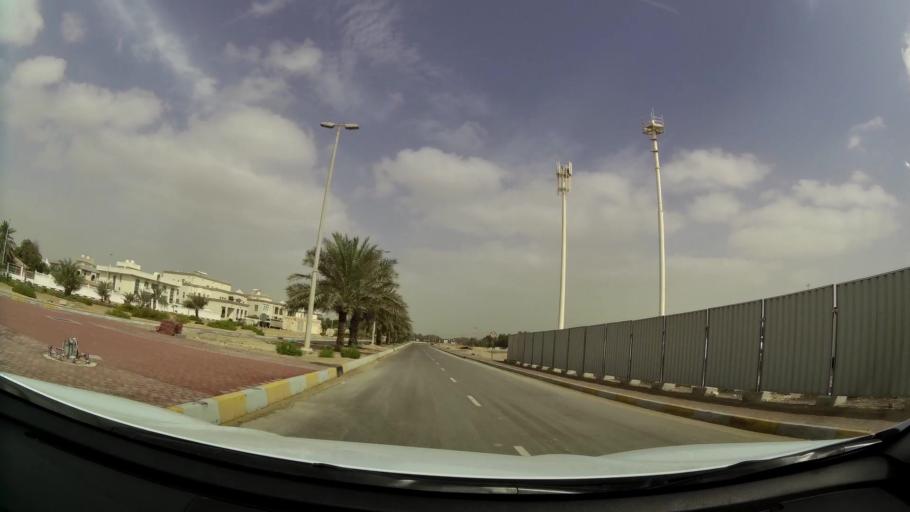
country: AE
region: Abu Dhabi
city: Abu Dhabi
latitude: 24.3973
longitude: 54.5223
